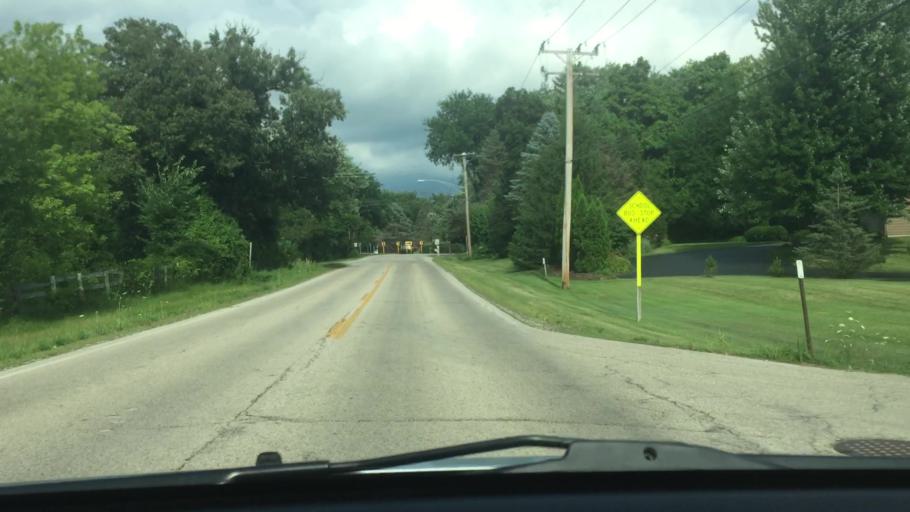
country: US
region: Illinois
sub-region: McHenry County
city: Lakewood
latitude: 42.2682
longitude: -88.3461
